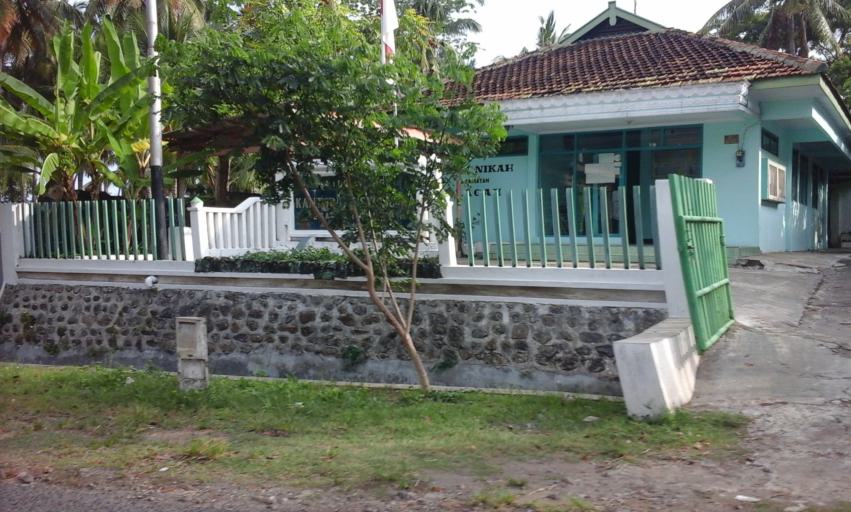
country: ID
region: East Java
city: Krajan
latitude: -8.2161
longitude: 114.3224
